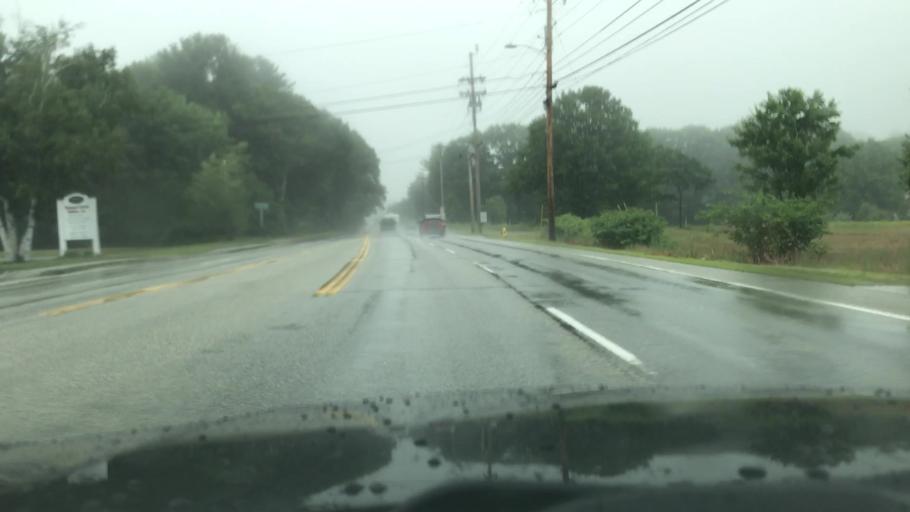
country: US
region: Maine
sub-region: Cumberland County
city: West Scarborough
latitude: 43.5584
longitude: -70.4011
